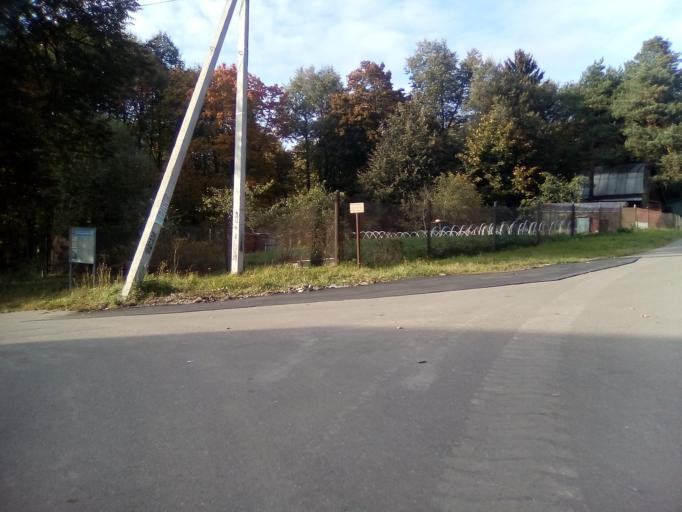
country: RU
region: Moskovskaya
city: Filimonki
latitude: 55.5530
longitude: 37.3537
